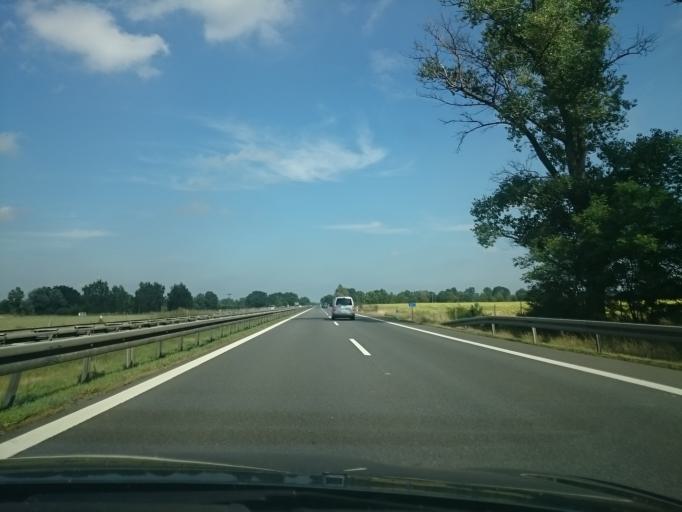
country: DE
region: Brandenburg
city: Calau
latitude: 51.7588
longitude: 13.8640
